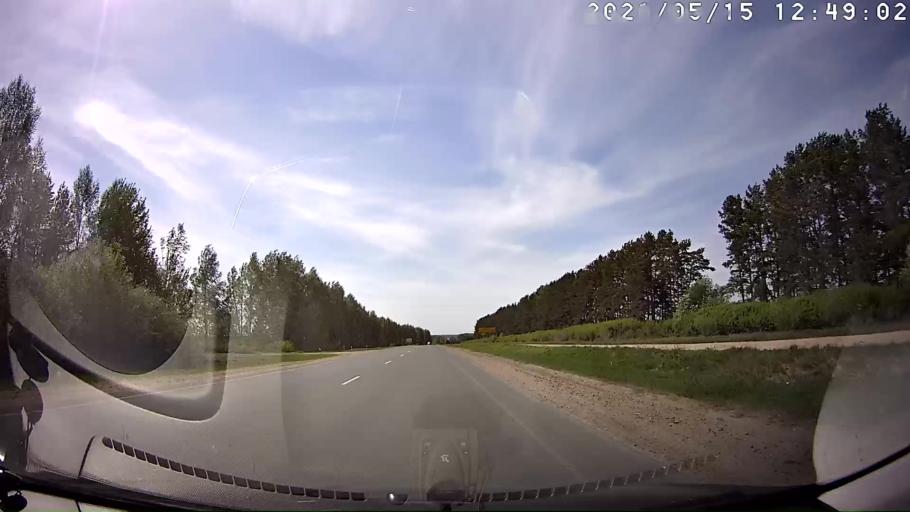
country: RU
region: Mariy-El
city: Sovetskiy
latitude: 56.7453
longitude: 48.2690
